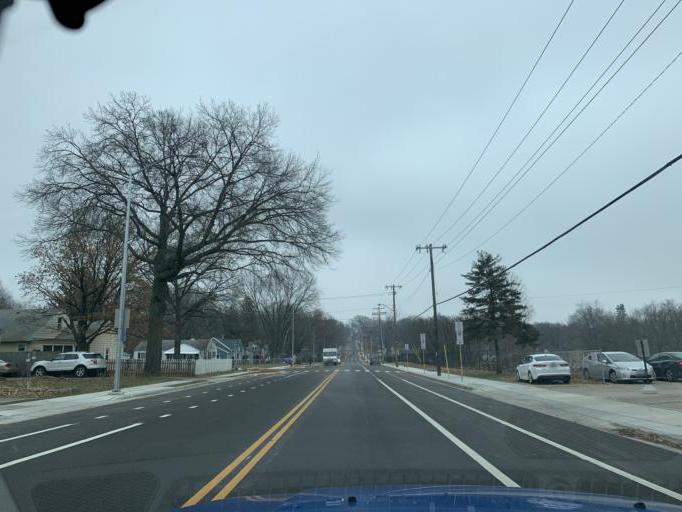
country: US
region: Wisconsin
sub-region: Dane County
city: Monona
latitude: 43.0774
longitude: -89.3207
